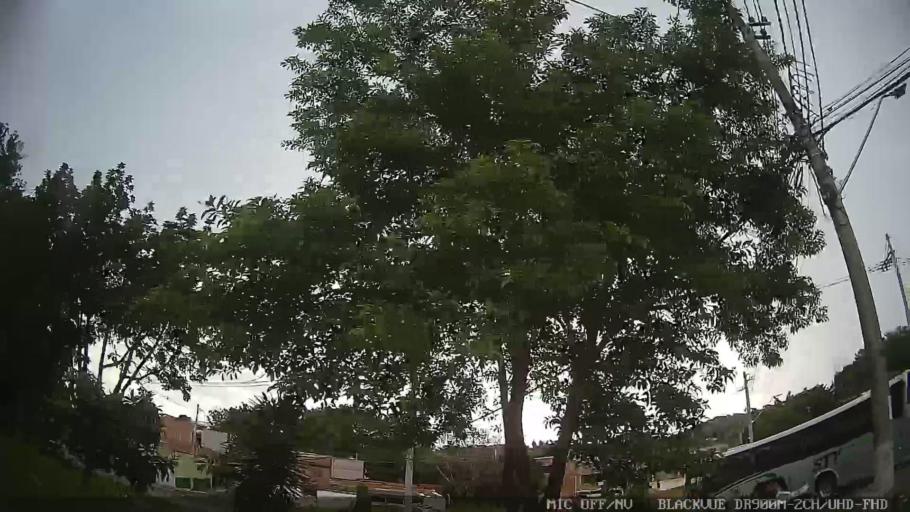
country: BR
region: Sao Paulo
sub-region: Pedreira
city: Pedreira
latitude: -22.7160
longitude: -46.8933
